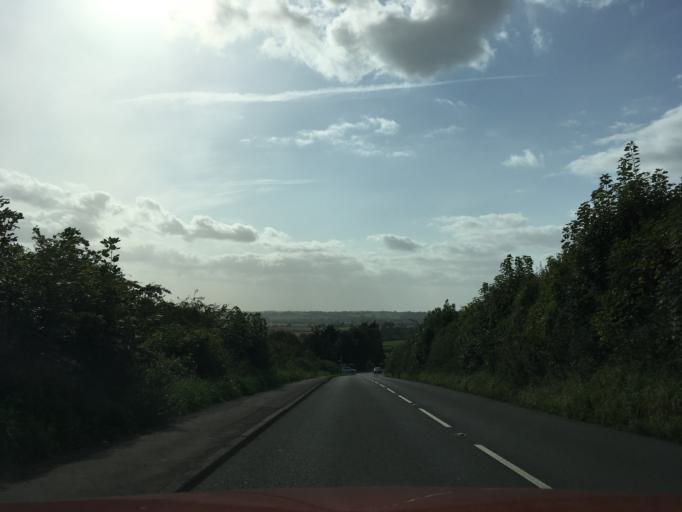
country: GB
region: England
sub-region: Gloucestershire
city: Wotton-under-Edge
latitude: 51.6355
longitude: -2.3578
